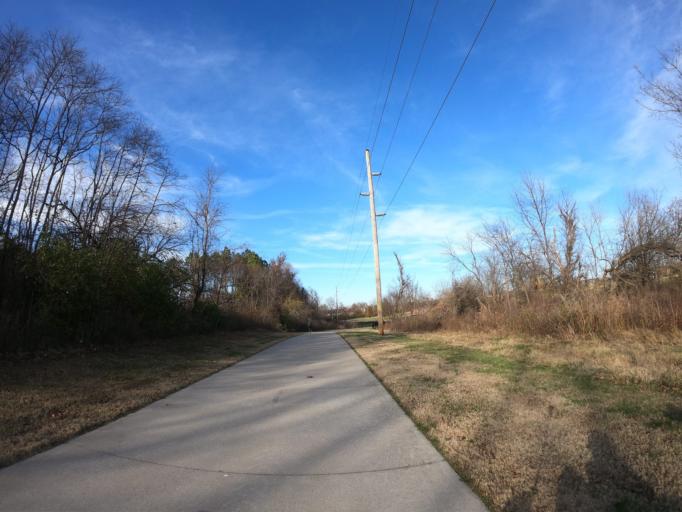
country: US
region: Arkansas
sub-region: Benton County
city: Lowell
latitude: 36.2849
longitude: -94.1663
